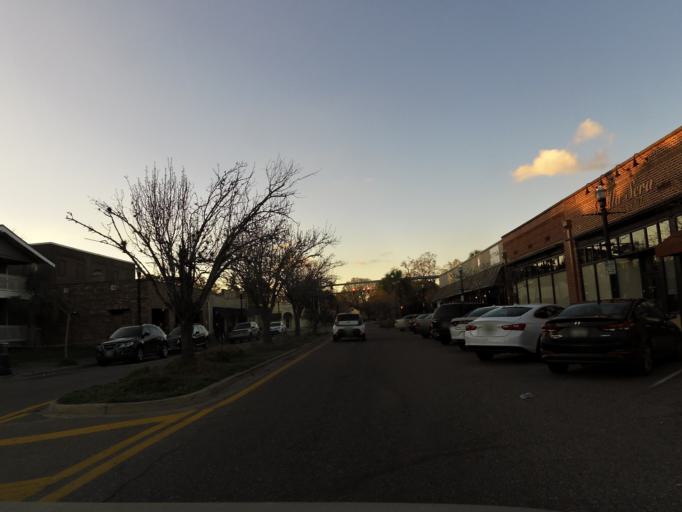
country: US
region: Florida
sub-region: Duval County
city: Jacksonville
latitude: 30.3136
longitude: -81.6958
